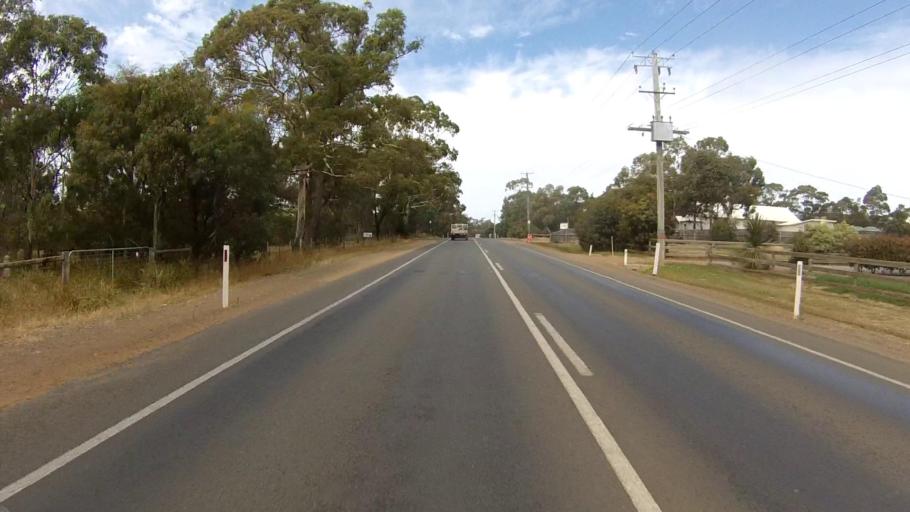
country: AU
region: Tasmania
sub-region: Clarence
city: Sandford
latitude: -42.9389
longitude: 147.4954
